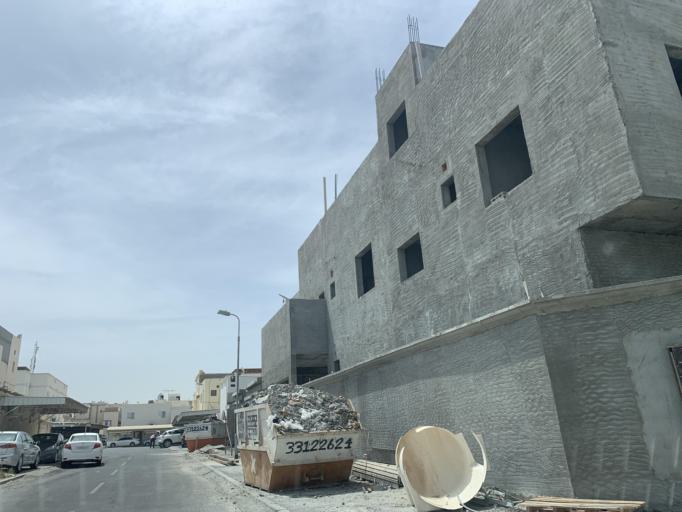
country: BH
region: Northern
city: Ar Rifa'
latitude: 26.1436
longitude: 50.5653
